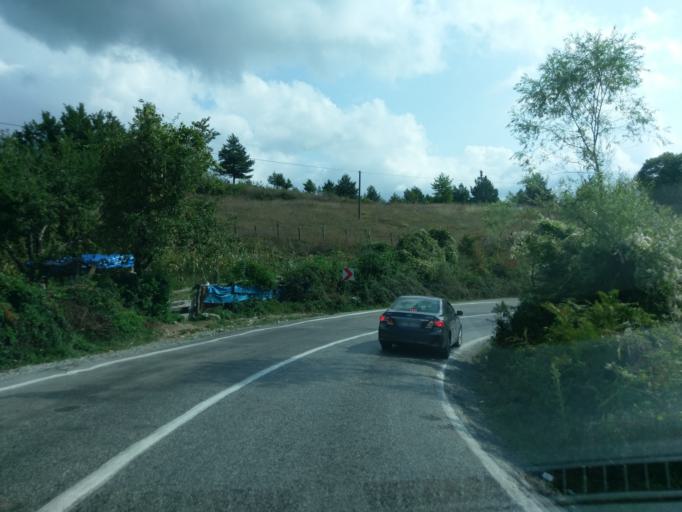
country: TR
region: Sinop
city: Yenikonak
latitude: 41.8773
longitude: 34.5432
